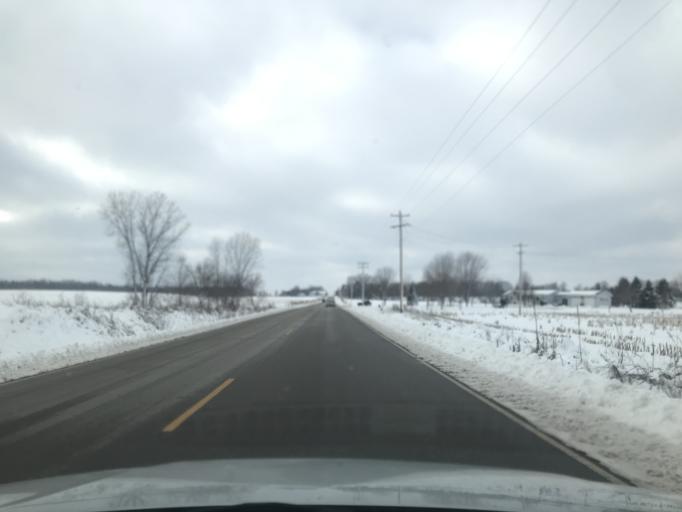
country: US
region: Wisconsin
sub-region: Oconto County
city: Oconto
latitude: 44.9499
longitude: -87.8944
